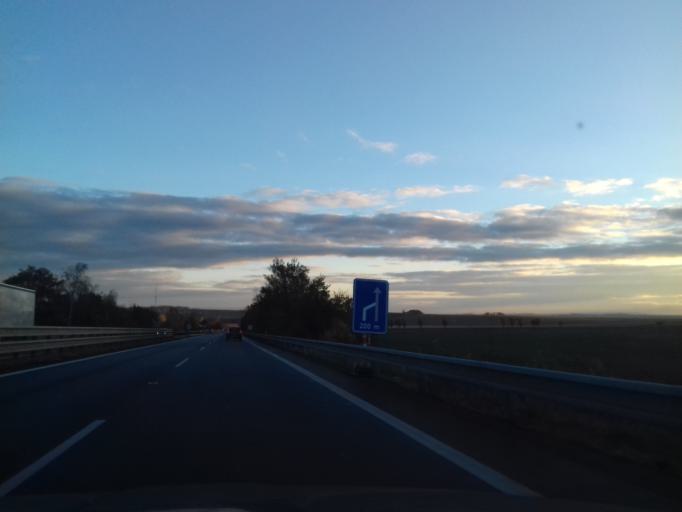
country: CZ
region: Olomoucky
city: Otaslavice
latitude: 49.3572
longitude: 17.0834
